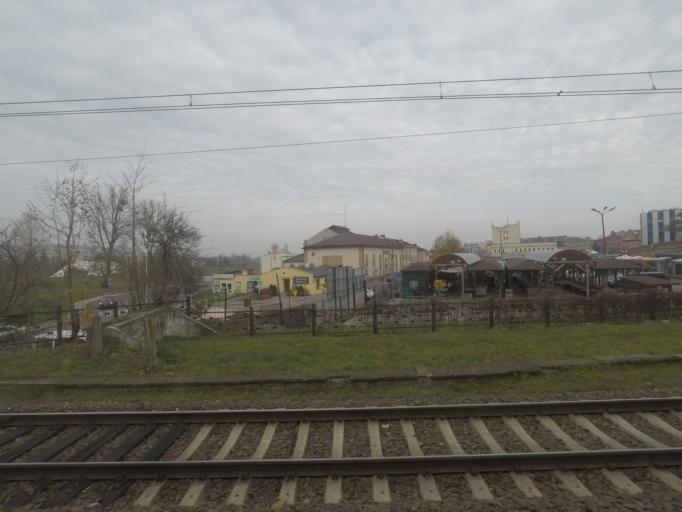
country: PL
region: Subcarpathian Voivodeship
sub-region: Przemysl
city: Przemysl
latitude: 49.7859
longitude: 22.7709
